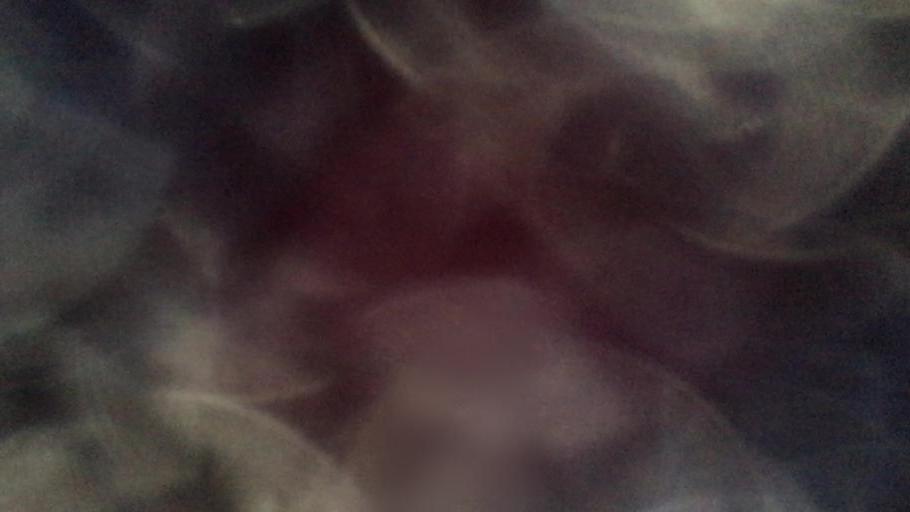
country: US
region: New Jersey
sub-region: Hudson County
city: Guttenberg
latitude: 40.7826
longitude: -73.9992
